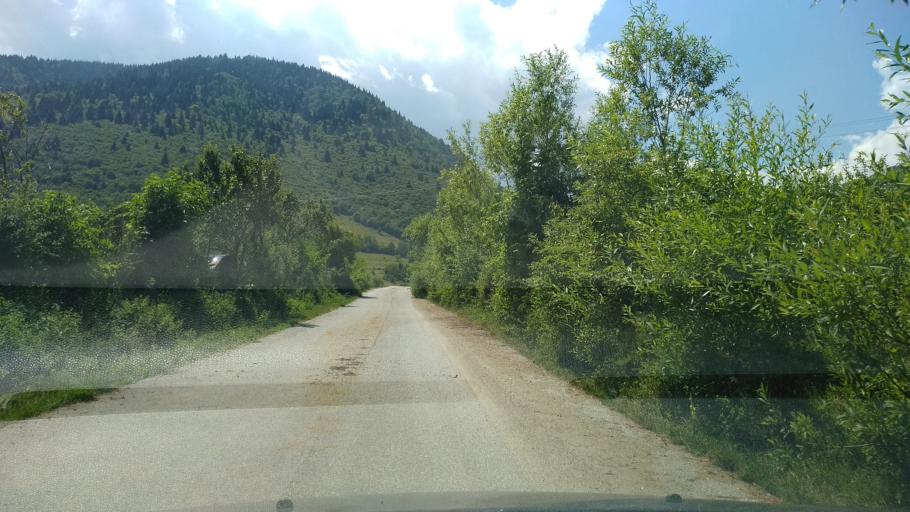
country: RO
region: Hunedoara
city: Salasu de Sus
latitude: 45.4777
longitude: 22.9085
